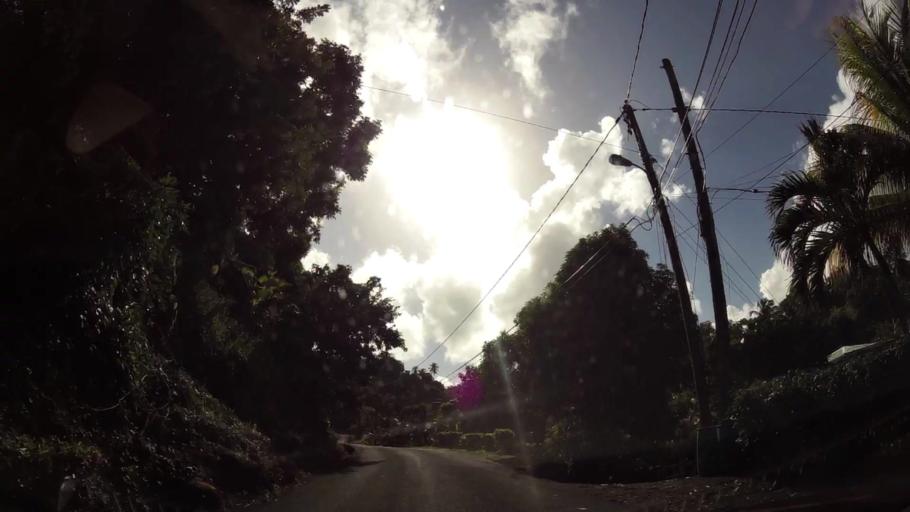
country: DM
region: Saint Andrew
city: Marigot
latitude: 15.5404
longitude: -61.2857
